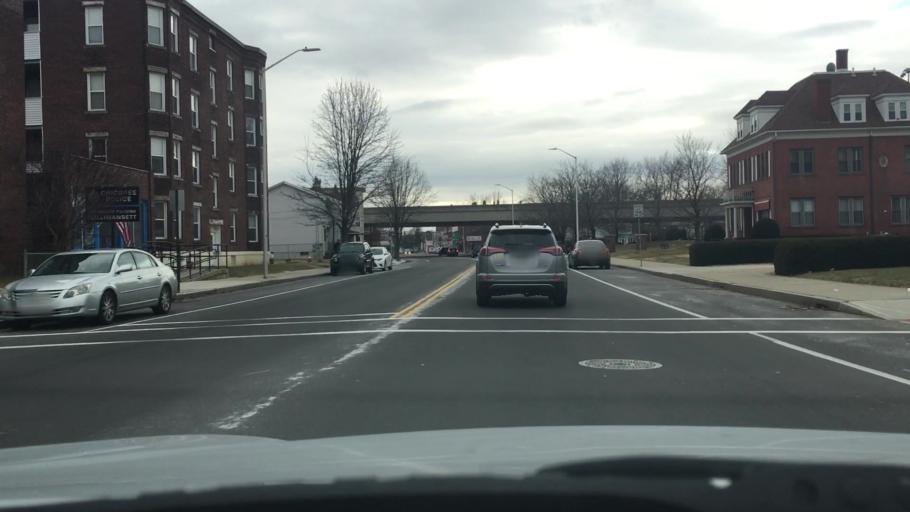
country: US
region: Massachusetts
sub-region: Hampden County
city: North Chicopee
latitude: 42.1880
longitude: -72.6064
